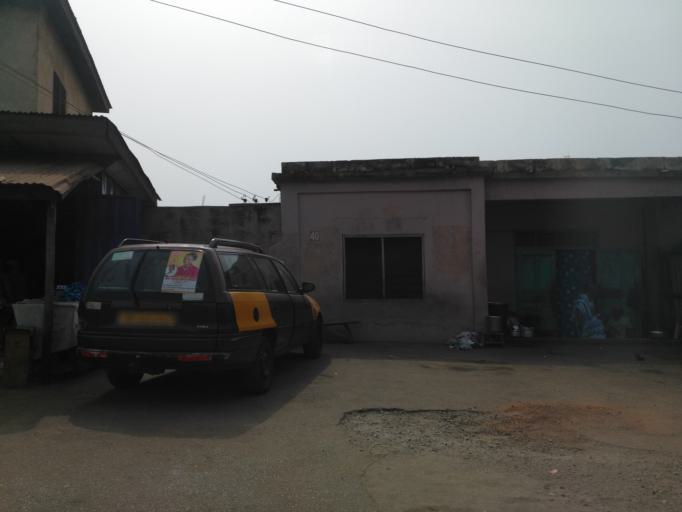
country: GH
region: Ashanti
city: Kumasi
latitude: 6.6988
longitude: -1.5978
